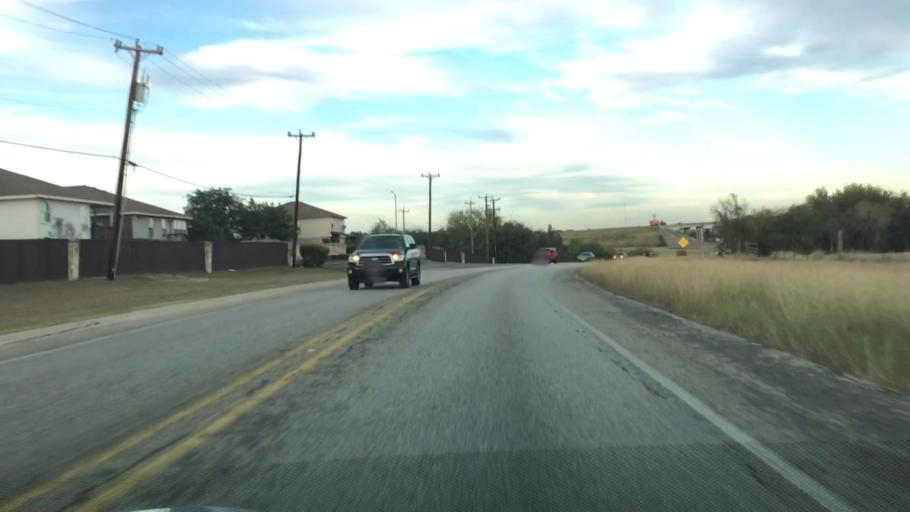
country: US
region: Texas
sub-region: Bexar County
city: Converse
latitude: 29.5308
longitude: -98.3060
